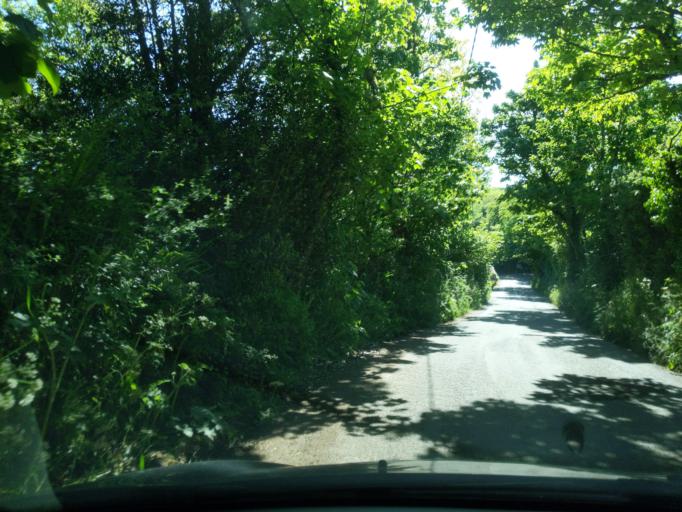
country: GB
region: England
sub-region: Cornwall
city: St. Buryan
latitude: 50.0578
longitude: -5.6212
